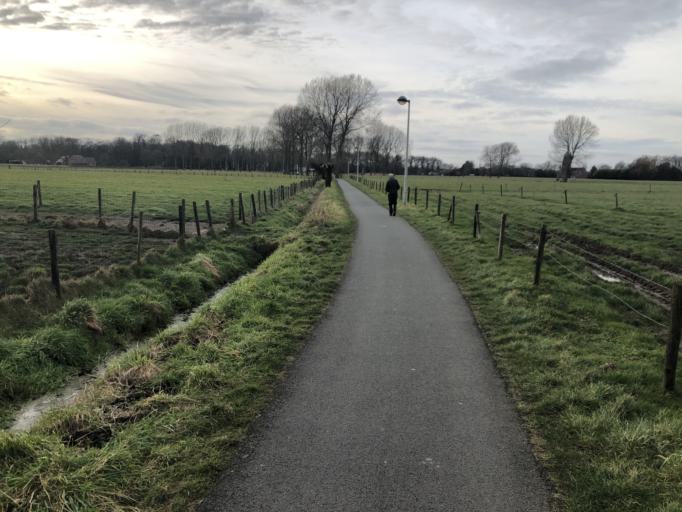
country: BE
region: Flanders
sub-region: Provincie Oost-Vlaanderen
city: Beveren
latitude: 51.2126
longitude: 4.2752
